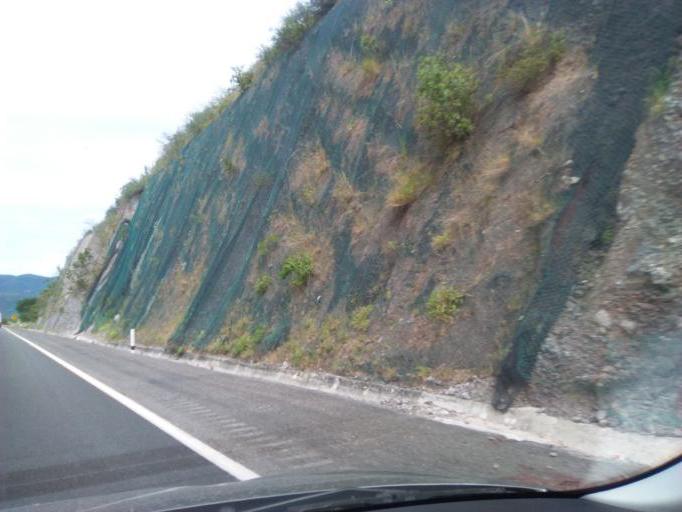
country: MX
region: Guerrero
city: Zumpango del Rio
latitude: 17.6192
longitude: -99.5185
